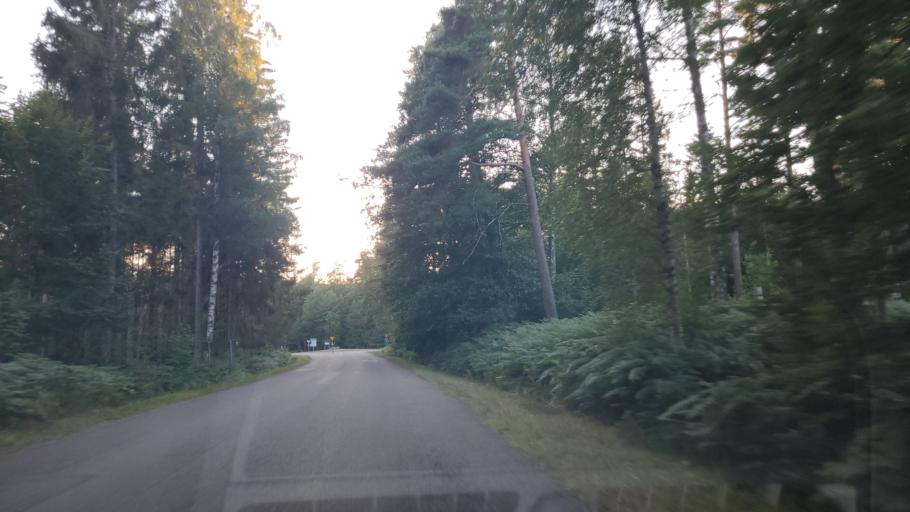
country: SE
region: Kalmar
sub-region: Borgholms Kommun
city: Borgholm
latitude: 57.2790
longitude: 17.0244
